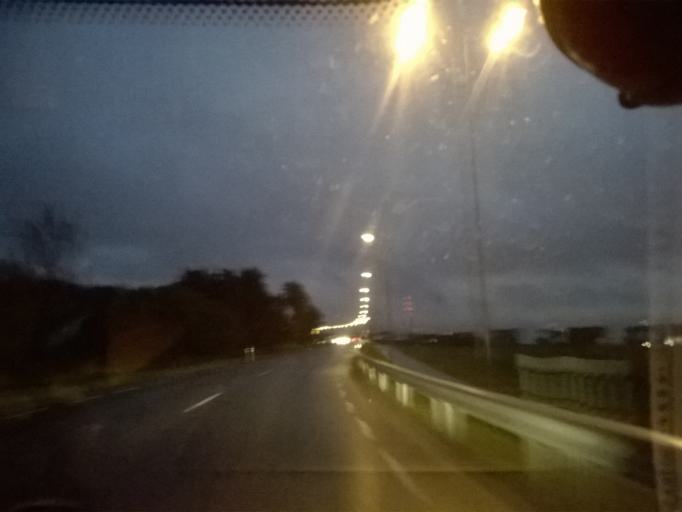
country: EE
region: Harju
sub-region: Viimsi vald
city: Viimsi
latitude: 59.5037
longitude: 24.8669
